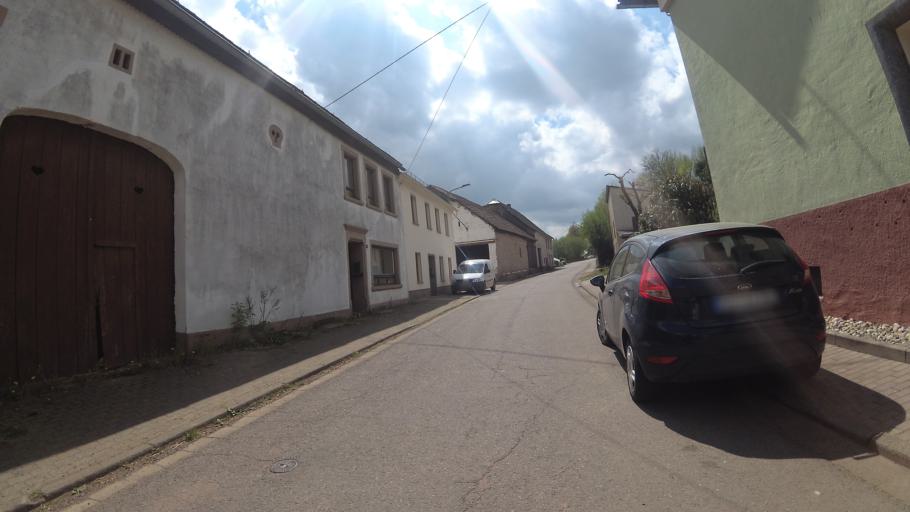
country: DE
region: Saarland
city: Nonnweiler
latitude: 49.5740
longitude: 6.9255
